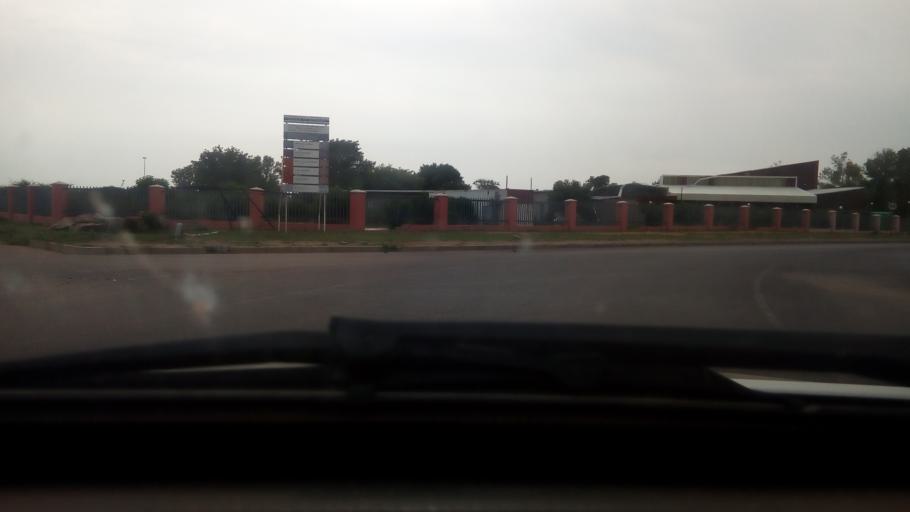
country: BW
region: South East
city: Gaborone
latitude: -24.6651
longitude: 25.9335
